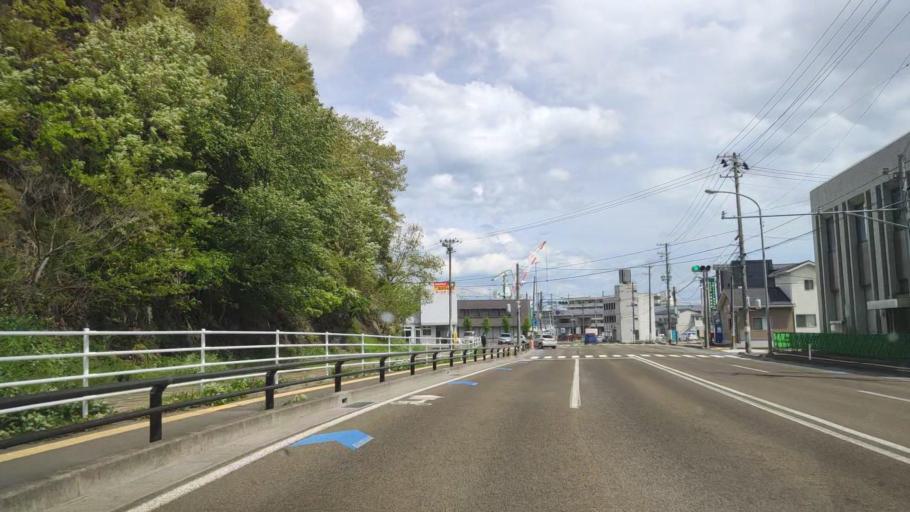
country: JP
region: Miyagi
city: Shiogama
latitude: 38.3244
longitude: 141.0257
